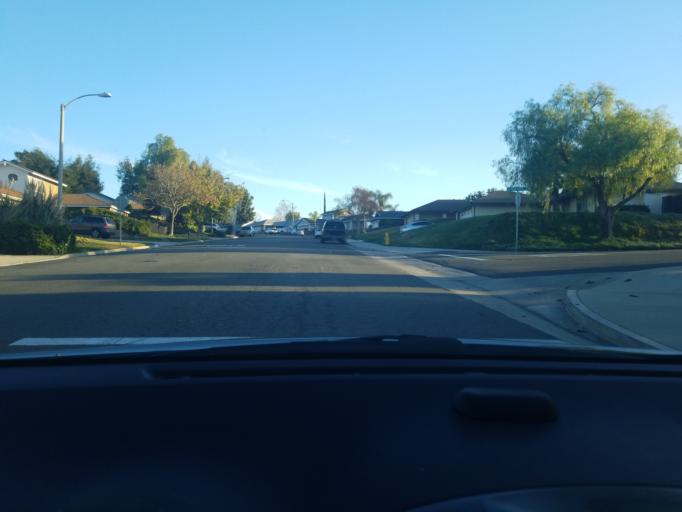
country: US
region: California
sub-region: Riverside County
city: Temecula
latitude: 33.5062
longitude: -117.1301
